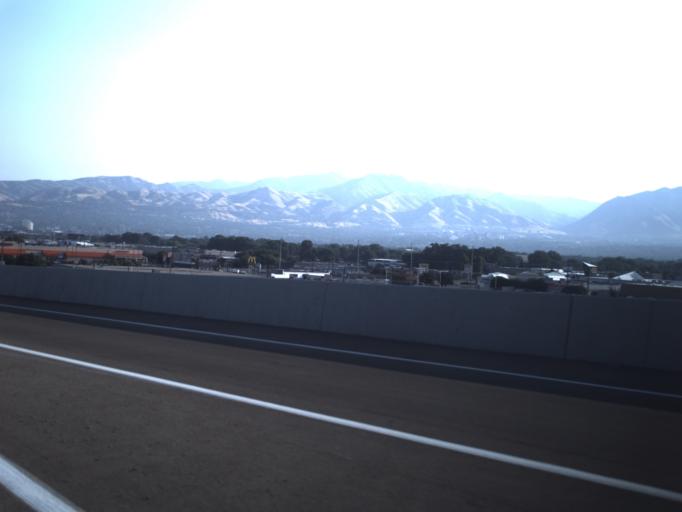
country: US
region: Utah
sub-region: Salt Lake County
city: South Salt Lake
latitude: 40.7216
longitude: -111.9033
